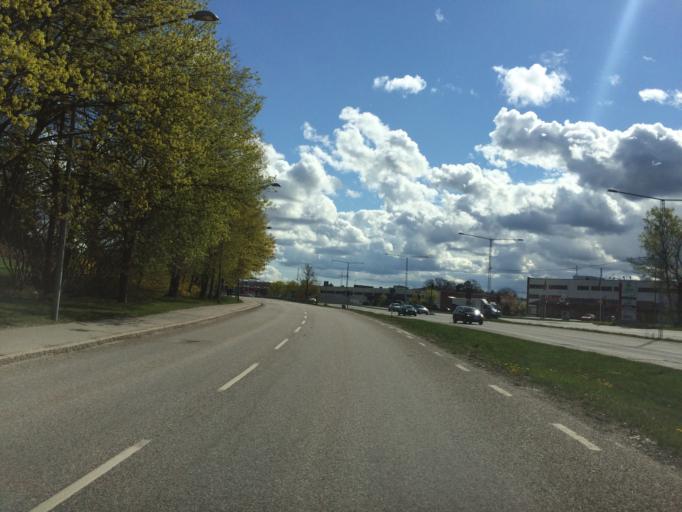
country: SE
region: Stockholm
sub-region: Huddinge Kommun
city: Segeltorp
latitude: 59.2884
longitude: 17.9360
